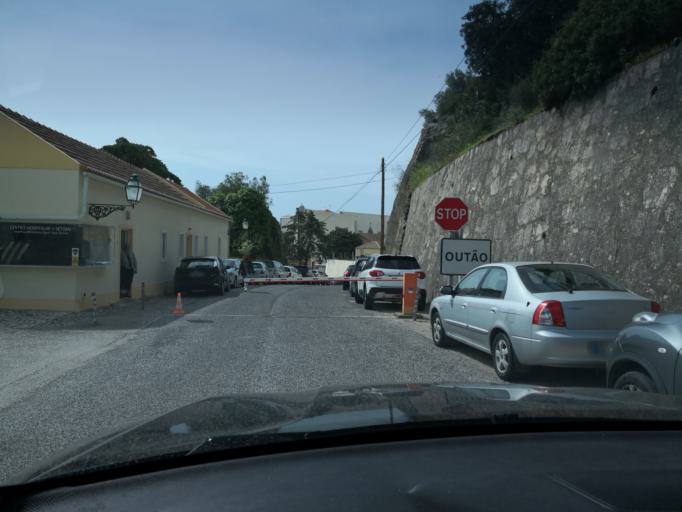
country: PT
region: Setubal
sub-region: Setubal
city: Setubal
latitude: 38.4904
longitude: -8.9342
